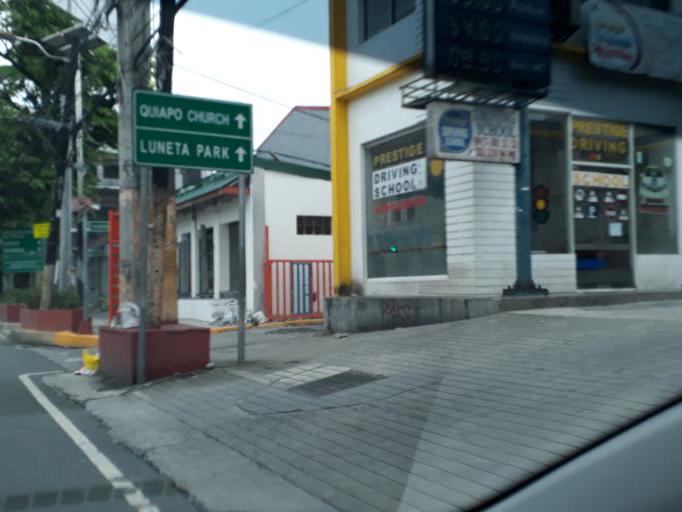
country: PH
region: Metro Manila
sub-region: City of Manila
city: Manila
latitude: 14.6140
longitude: 120.9973
